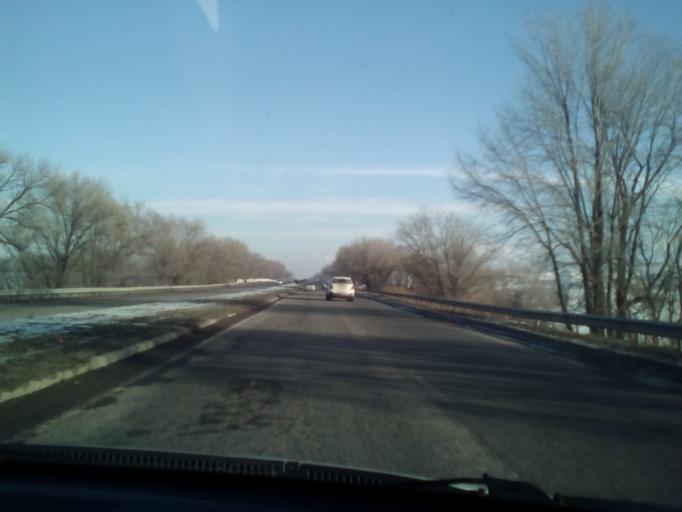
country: KZ
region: Almaty Oblysy
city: Burunday
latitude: 43.2214
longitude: 76.4432
